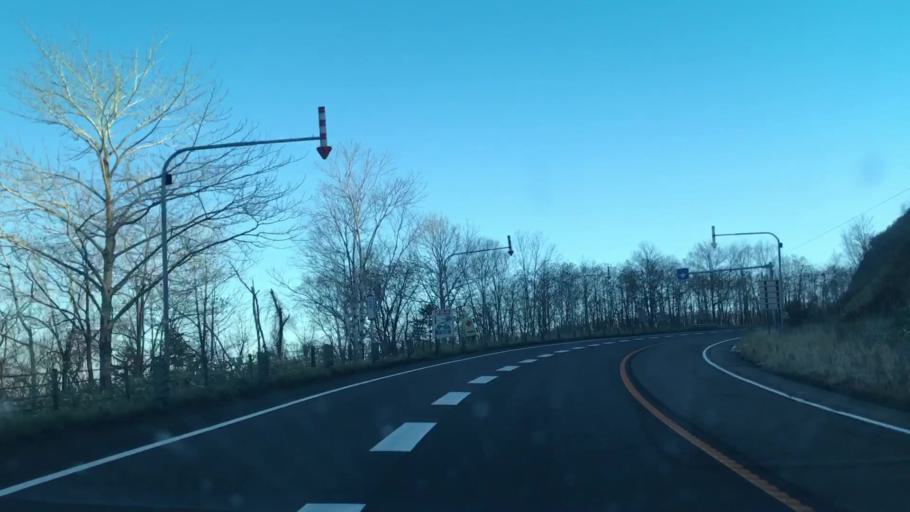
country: JP
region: Hokkaido
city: Otofuke
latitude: 42.9745
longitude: 142.8008
